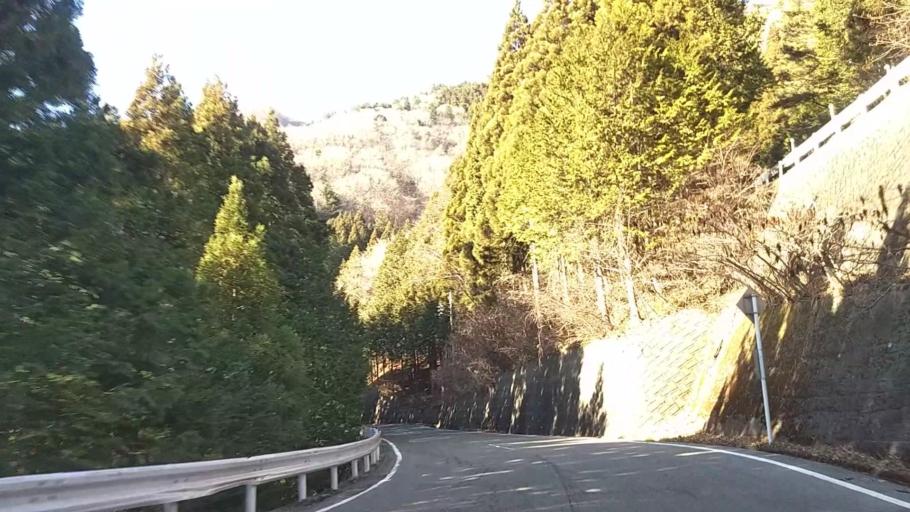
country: JP
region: Yamanashi
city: Otsuki
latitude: 35.5119
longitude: 138.9832
